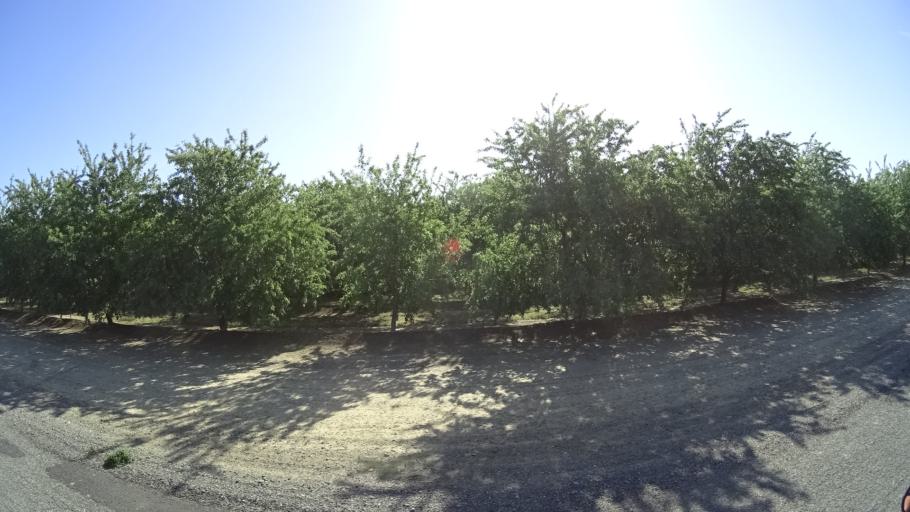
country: US
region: California
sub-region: Glenn County
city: Hamilton City
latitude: 39.6927
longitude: -122.0641
